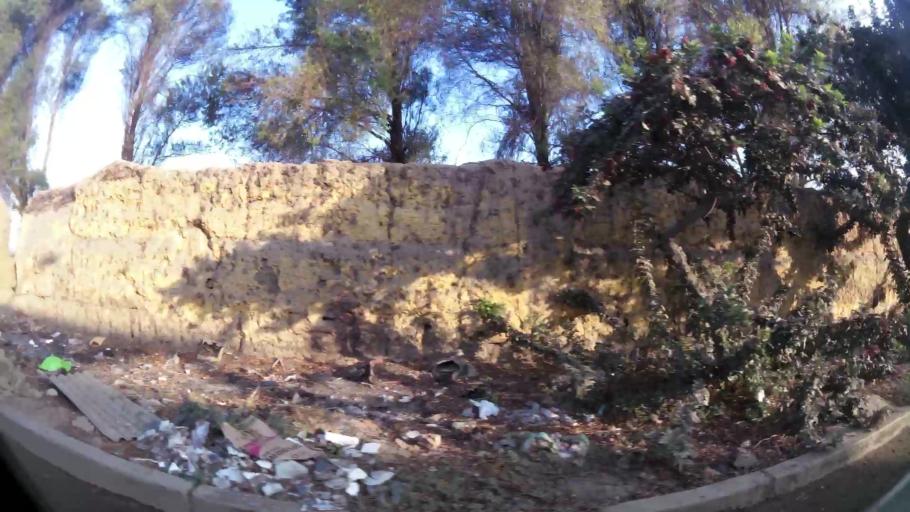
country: PE
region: La Libertad
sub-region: Provincia de Trujillo
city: El Porvenir
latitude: -8.0931
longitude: -78.9948
